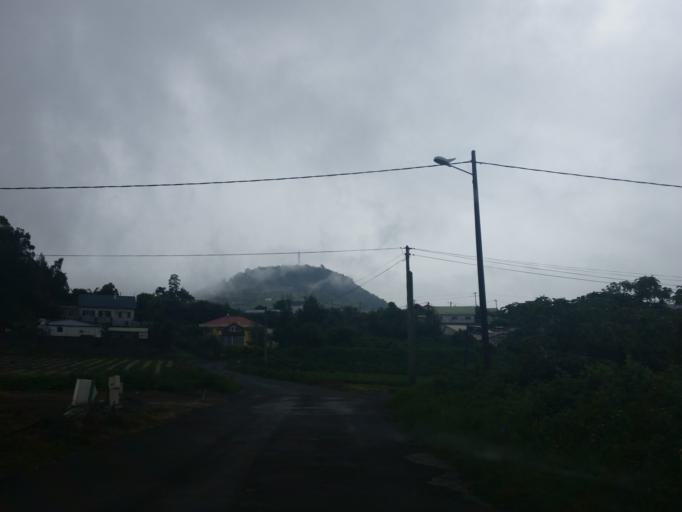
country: RE
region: Reunion
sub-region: Reunion
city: Le Tampon
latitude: -21.2283
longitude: 55.5272
